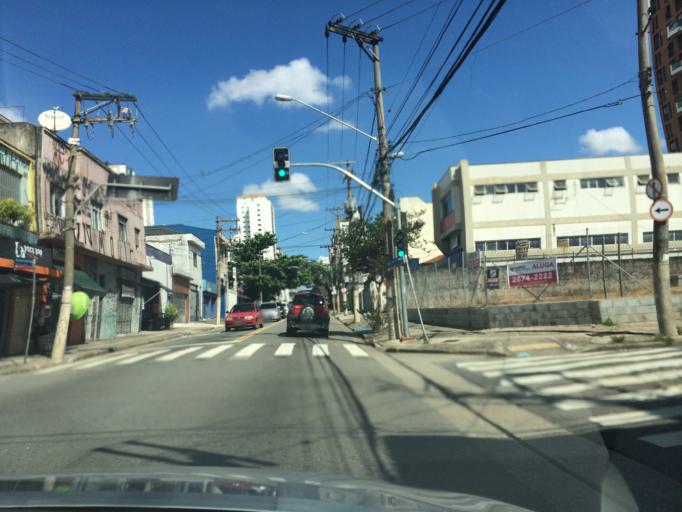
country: BR
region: Sao Paulo
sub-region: Sao Caetano Do Sul
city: Sao Caetano do Sul
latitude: -23.5477
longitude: -46.5552
